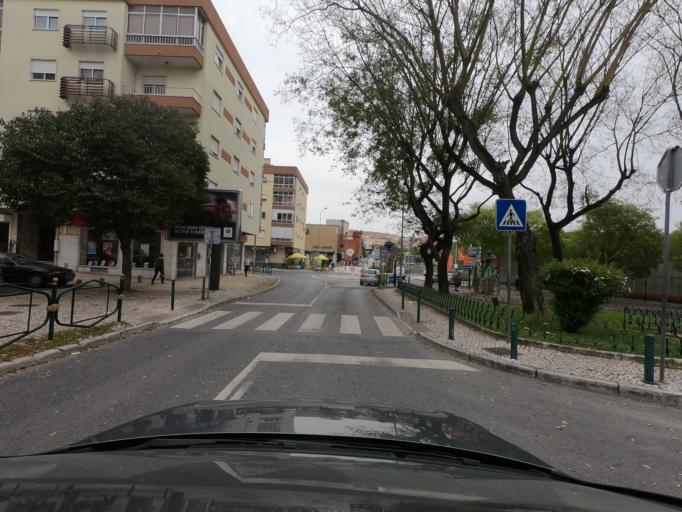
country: PT
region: Lisbon
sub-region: Sintra
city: Queluz
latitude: 38.7565
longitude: -9.2497
